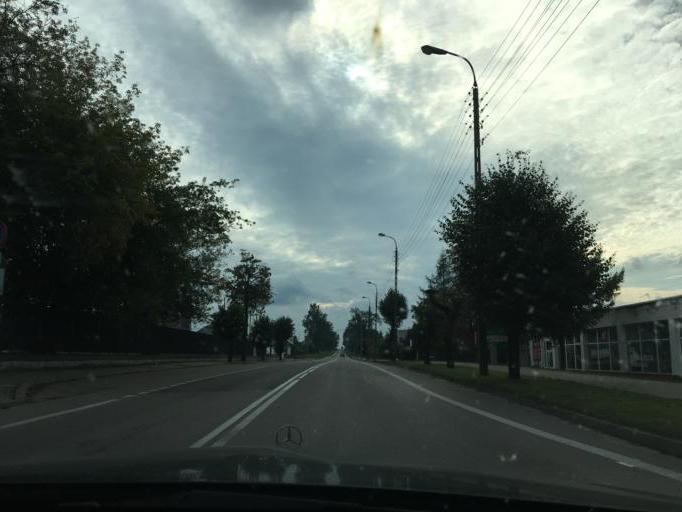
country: PL
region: Podlasie
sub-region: Powiat grajewski
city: Grajewo
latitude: 53.6439
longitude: 22.4479
